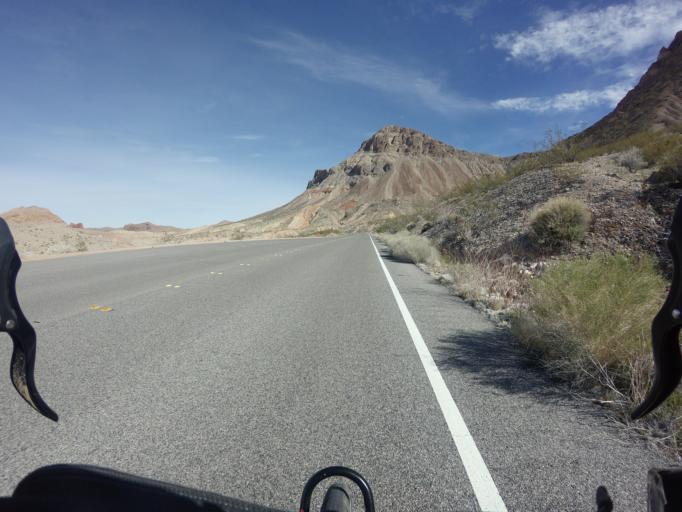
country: US
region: Nevada
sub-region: Clark County
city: Boulder City
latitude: 36.2156
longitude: -114.6382
